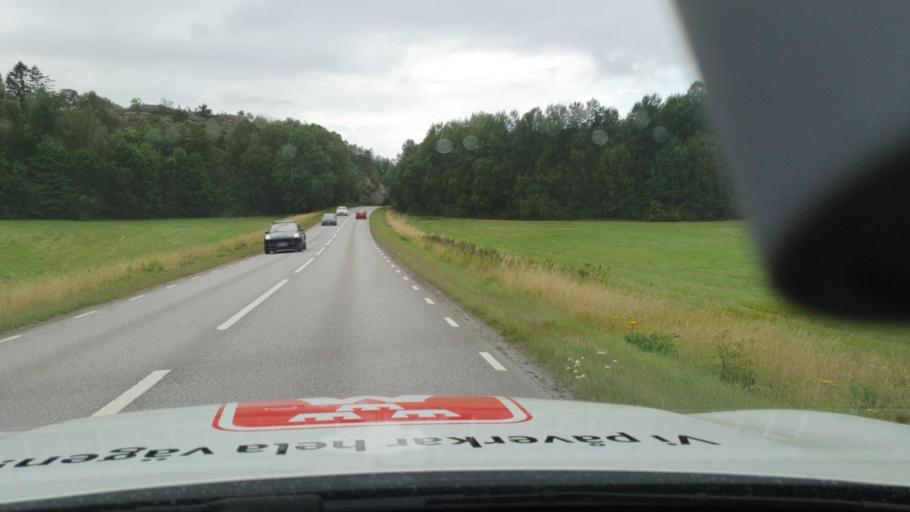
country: SE
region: Vaestra Goetaland
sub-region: Sotenas Kommun
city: Hunnebostrand
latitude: 58.4590
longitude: 11.3300
